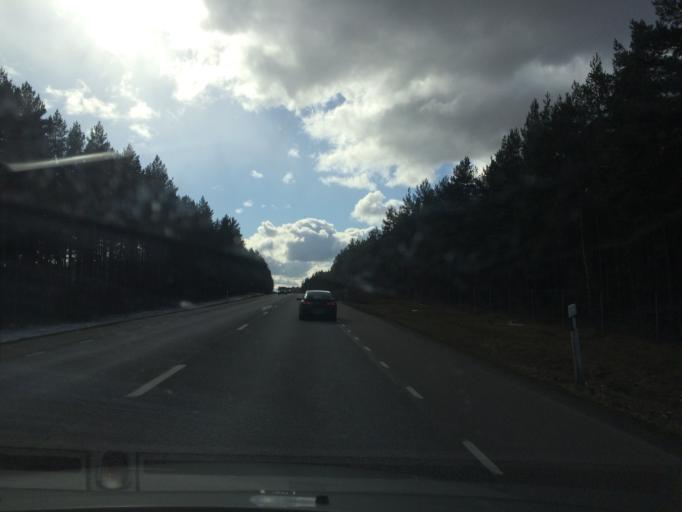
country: SE
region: Vaestra Goetaland
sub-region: Gotene Kommun
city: Goetene
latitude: 58.6117
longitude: 13.6519
